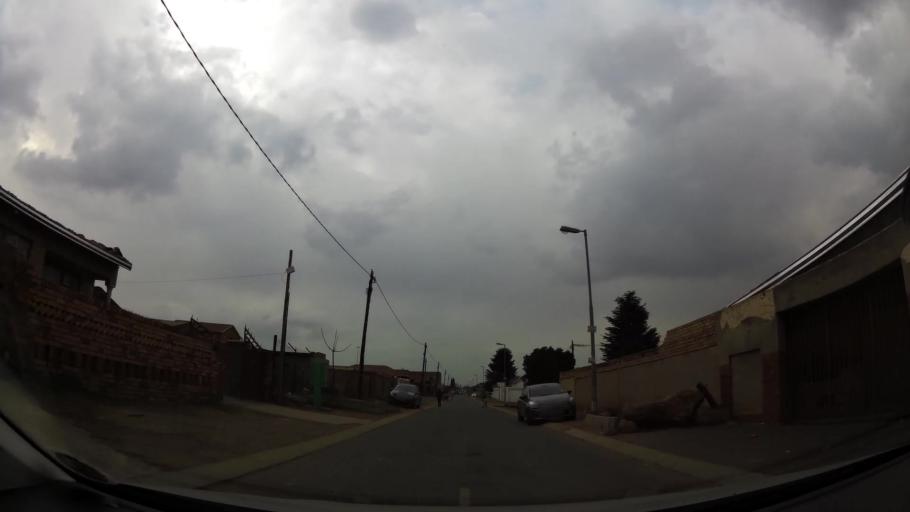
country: ZA
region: Gauteng
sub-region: City of Johannesburg Metropolitan Municipality
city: Soweto
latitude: -26.2653
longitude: 27.8638
